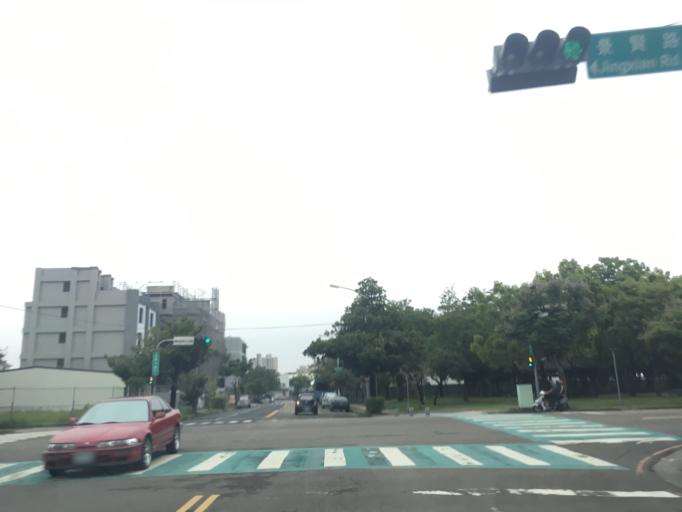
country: TW
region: Taiwan
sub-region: Taichung City
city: Taichung
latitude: 24.1669
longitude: 120.7120
